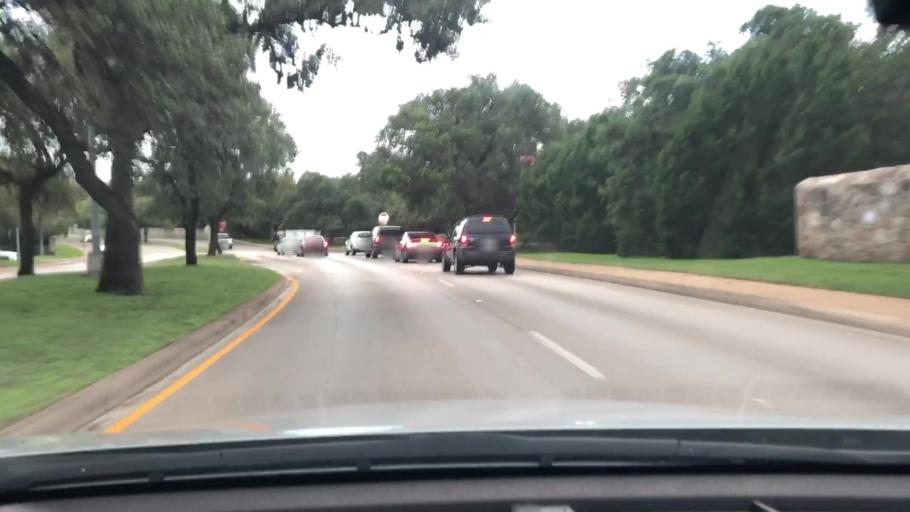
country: US
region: Texas
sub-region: Bexar County
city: Shavano Park
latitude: 29.5951
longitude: -98.5338
